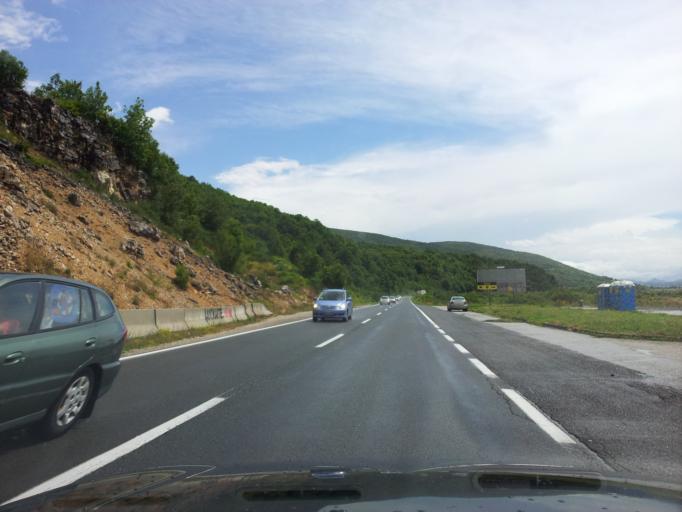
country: BA
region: Federation of Bosnia and Herzegovina
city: Bihac
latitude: 44.6258
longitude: 15.7354
